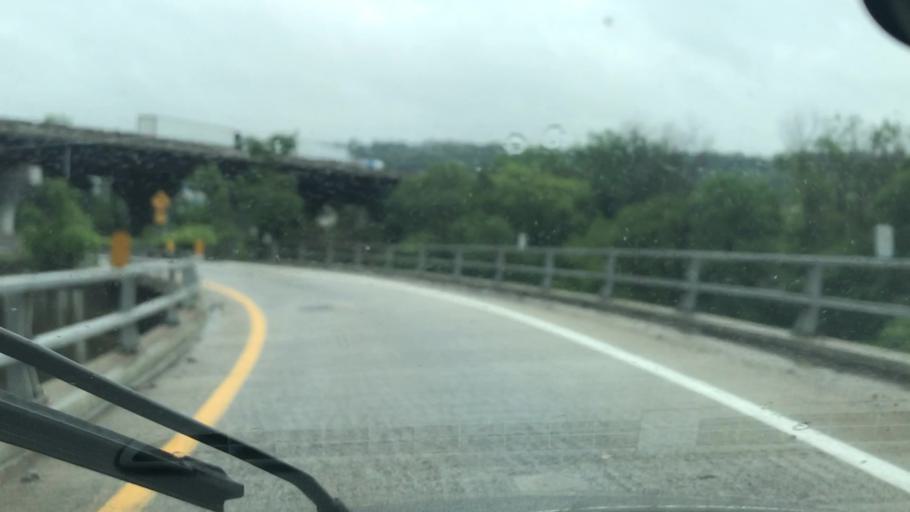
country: US
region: New York
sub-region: Westchester County
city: Elmsford
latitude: 41.0580
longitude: -73.8225
